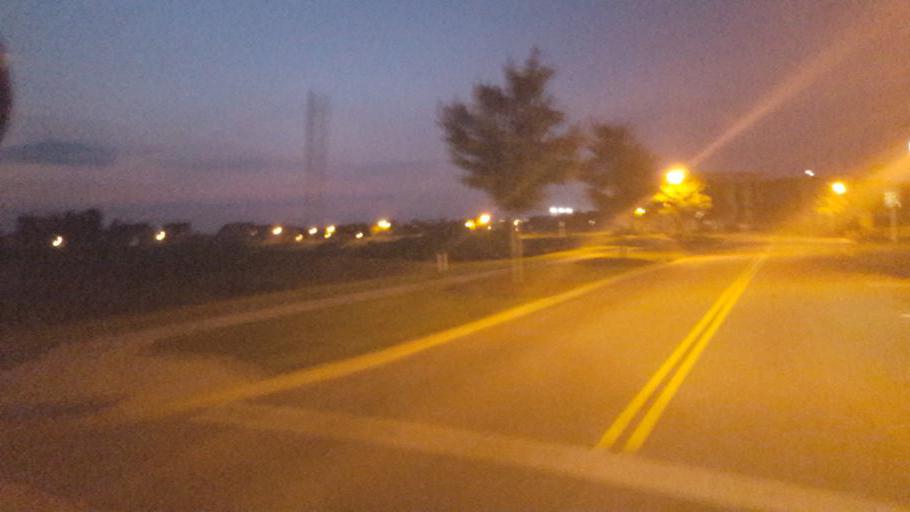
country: US
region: South Carolina
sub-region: York County
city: Fort Mill
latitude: 34.9777
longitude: -80.9782
